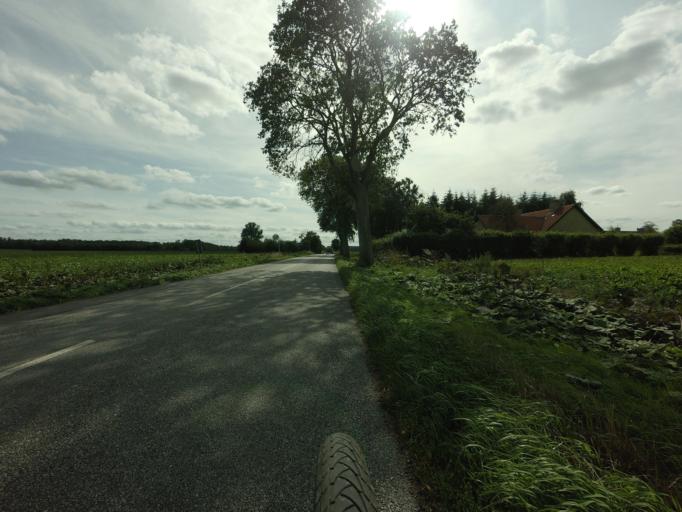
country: DK
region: Zealand
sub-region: Faxe Kommune
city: Fakse Ladeplads
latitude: 55.2517
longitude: 12.2234
